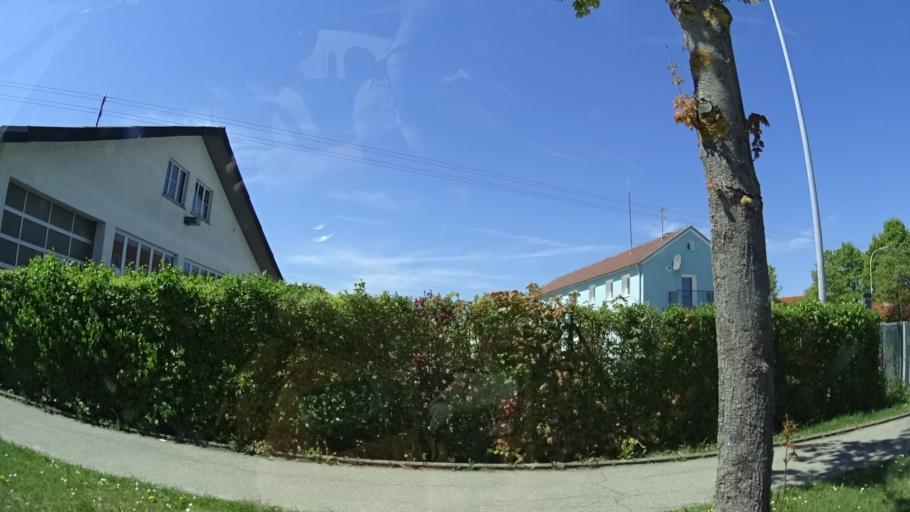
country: DE
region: Baden-Wuerttemberg
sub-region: Freiburg Region
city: Zimmern ob Rottweil
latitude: 48.1655
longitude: 8.6011
